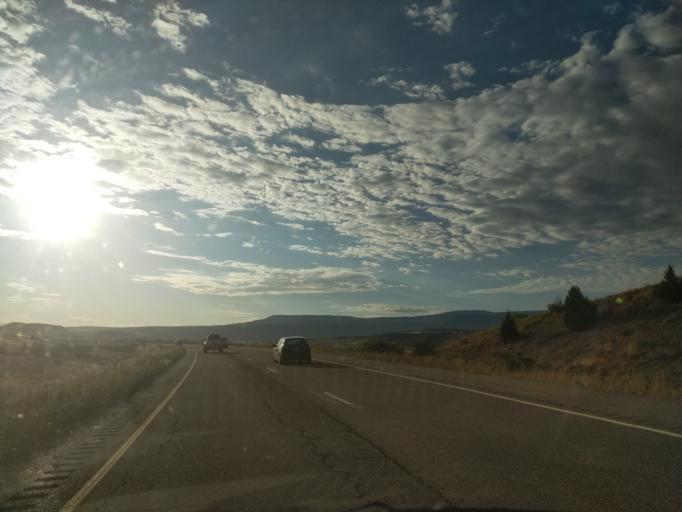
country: US
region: Colorado
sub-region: Garfield County
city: Battlement Mesa
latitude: 39.4987
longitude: -107.9212
